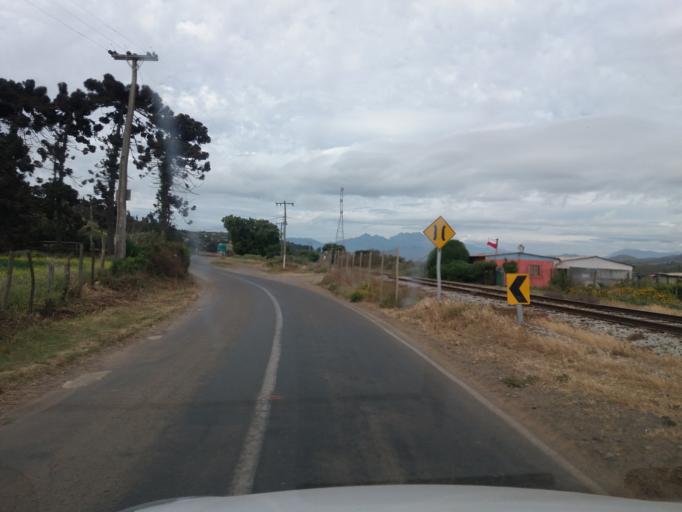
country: CL
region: Valparaiso
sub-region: Provincia de Marga Marga
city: Villa Alemana
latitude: -32.9168
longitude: -71.4040
